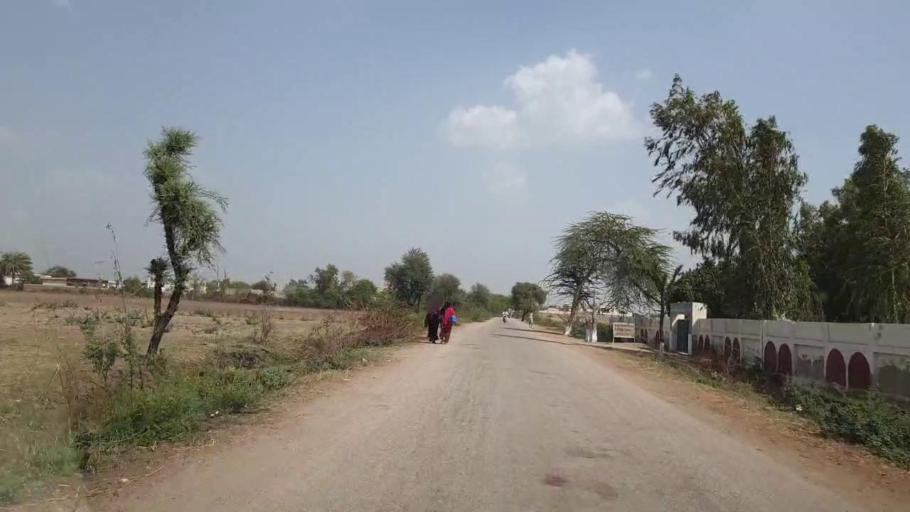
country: PK
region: Sindh
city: Tando Ghulam Ali
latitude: 25.0646
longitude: 68.8276
